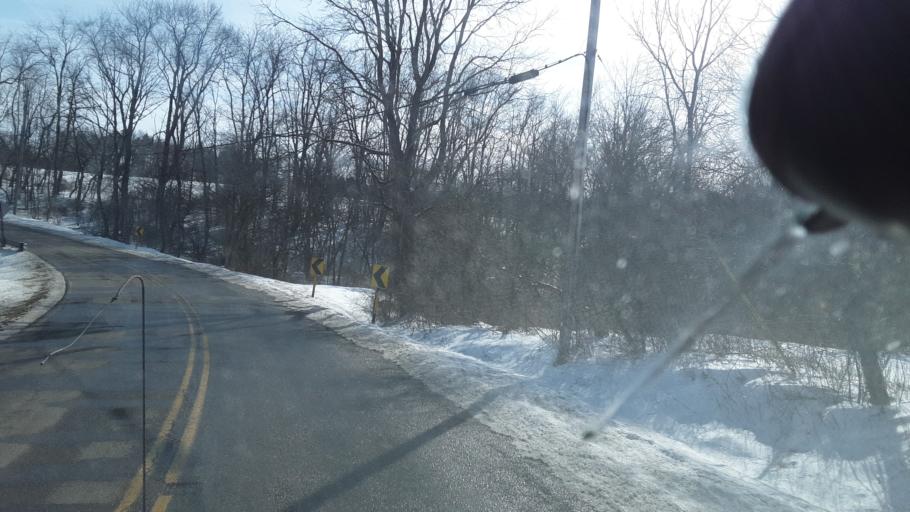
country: US
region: Ohio
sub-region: Columbiana County
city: Columbiana
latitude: 40.9537
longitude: -80.6986
